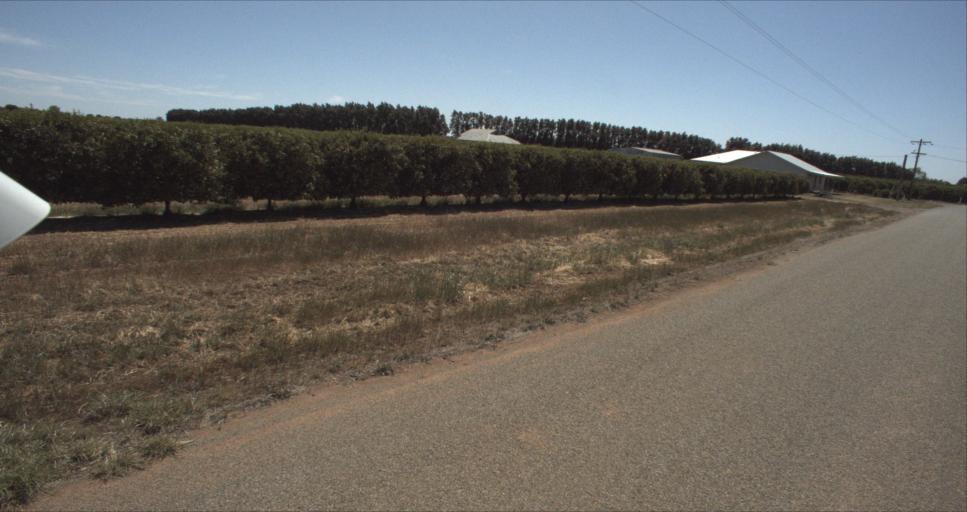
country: AU
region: New South Wales
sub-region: Leeton
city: Leeton
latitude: -34.5396
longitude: 146.3522
